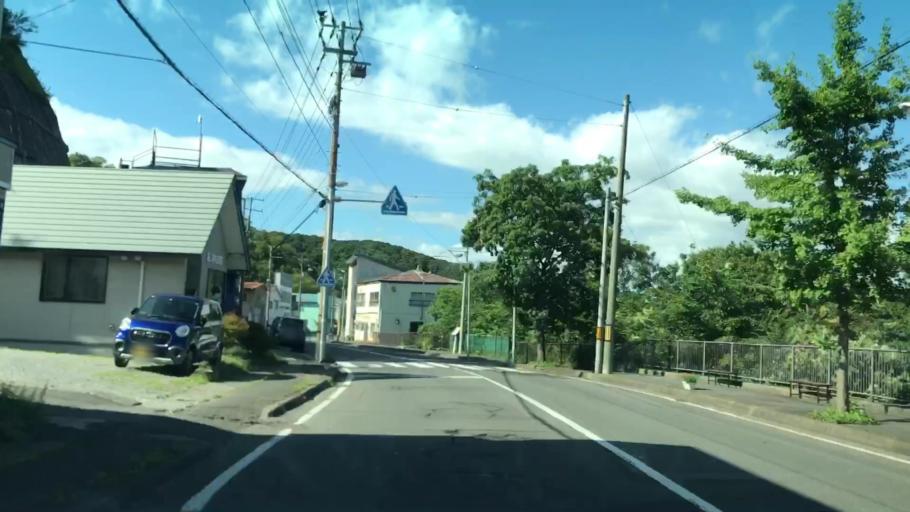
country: JP
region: Hokkaido
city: Muroran
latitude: 42.3228
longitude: 140.9687
